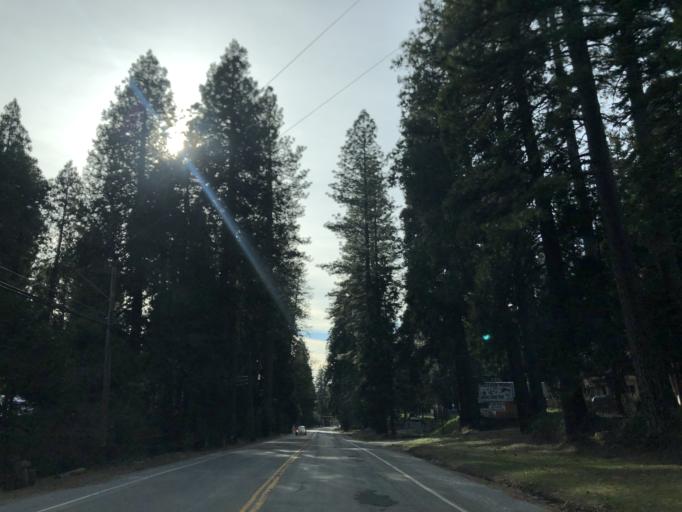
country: US
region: California
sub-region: El Dorado County
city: Pollock Pines
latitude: 38.7519
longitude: -120.6074
